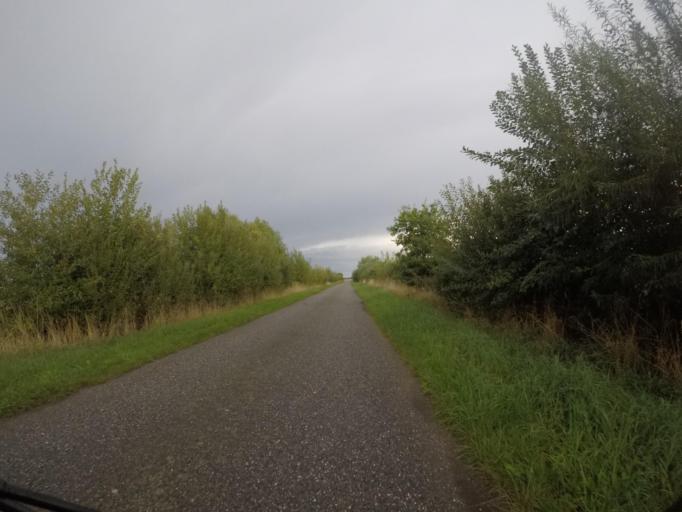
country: DE
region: Lower Saxony
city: Neu Darchau
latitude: 53.2536
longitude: 10.8951
